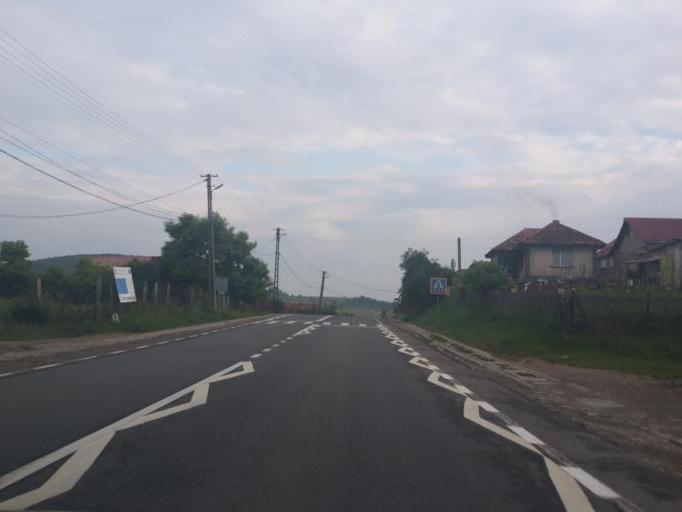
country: RO
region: Cluj
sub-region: Comuna Sanpaul
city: Sanpaul
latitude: 46.9039
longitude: 23.4175
